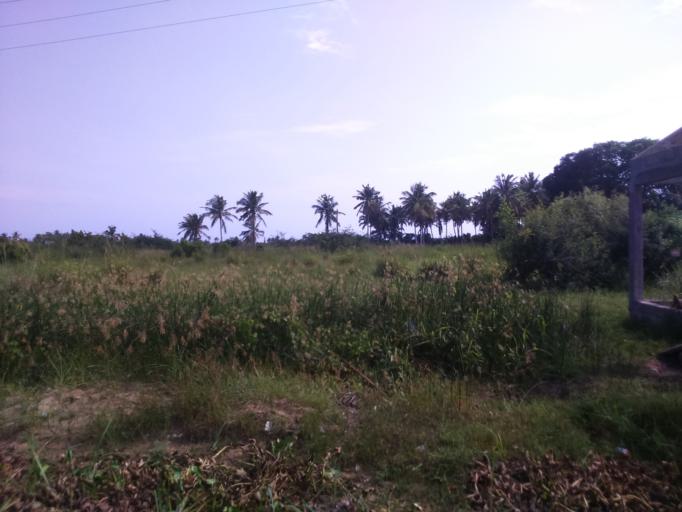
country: BJ
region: Mono
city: Grand-Popo
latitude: 6.2868
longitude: 1.8086
